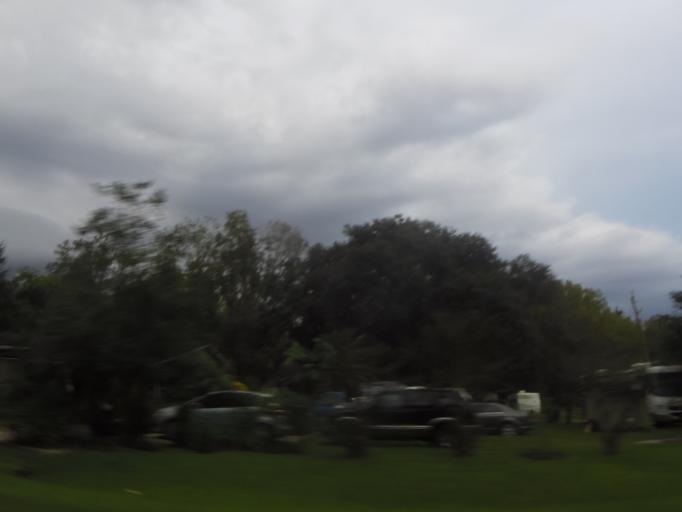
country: US
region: Florida
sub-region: Clay County
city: Bellair-Meadowbrook Terrace
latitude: 30.2843
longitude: -81.7959
